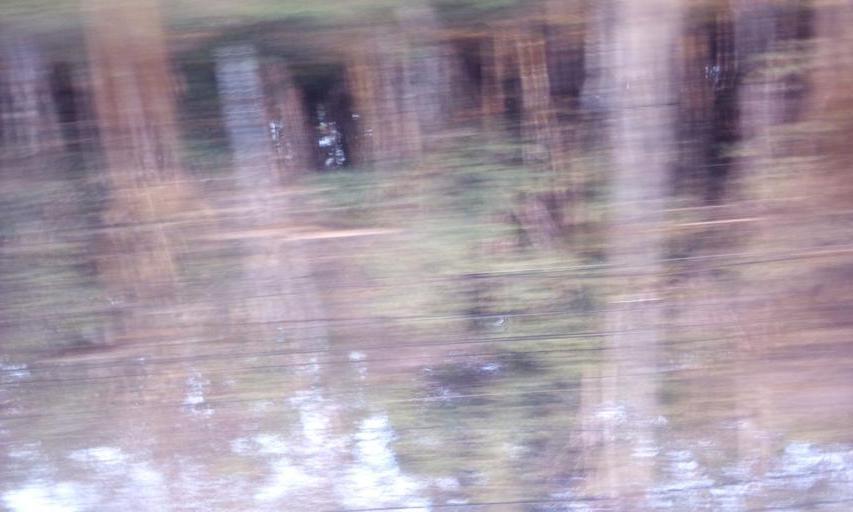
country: TH
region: Trat
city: Khao Saming
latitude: 12.3487
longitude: 102.3788
